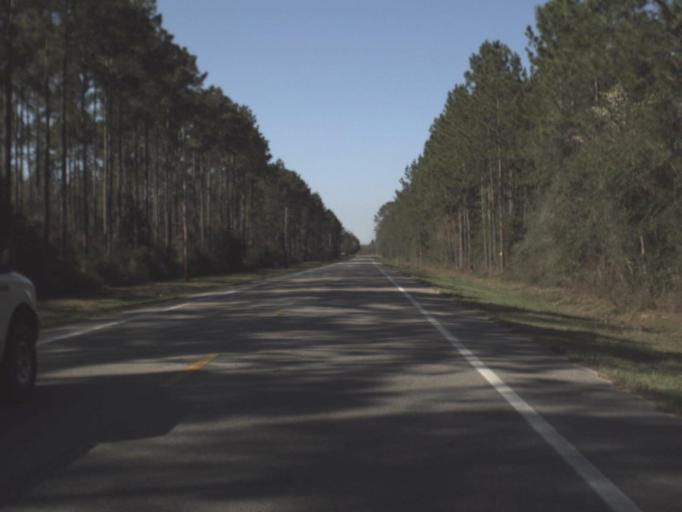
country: US
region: Florida
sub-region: Gulf County
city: Wewahitchka
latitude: 30.1907
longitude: -85.2066
